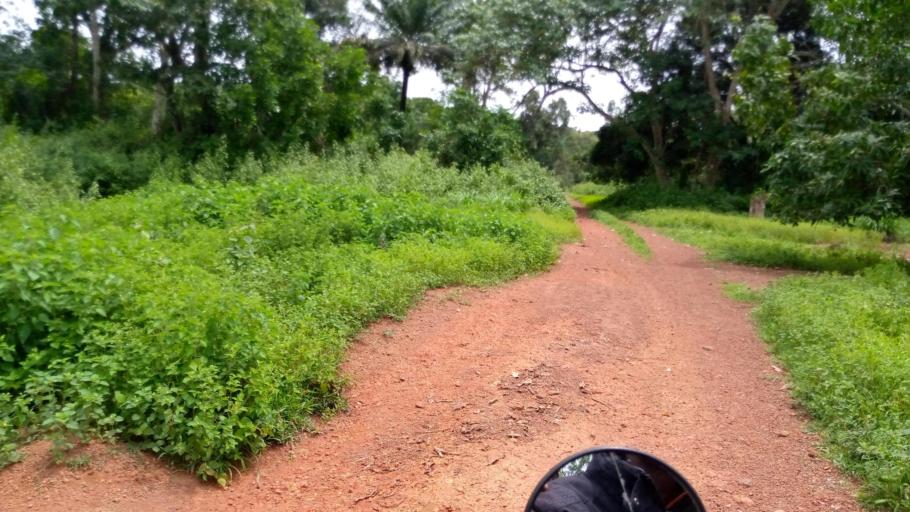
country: SL
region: Southern Province
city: Rotifunk
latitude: 8.1939
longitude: -12.5675
